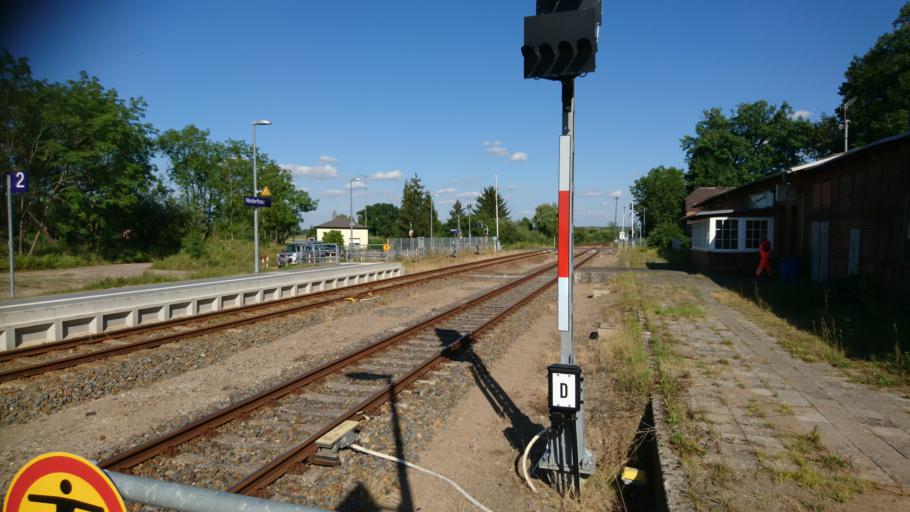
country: DE
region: Brandenburg
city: Niederfinow
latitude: 52.8307
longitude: 13.9284
